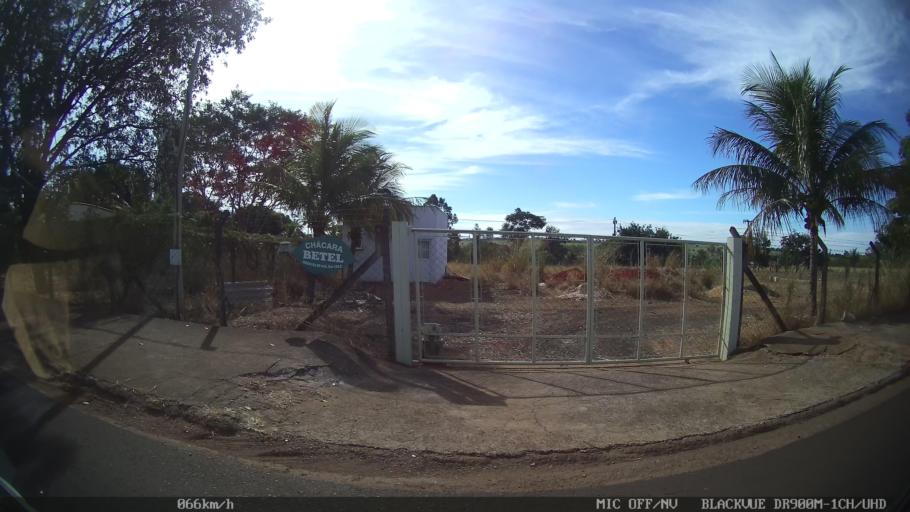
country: BR
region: Sao Paulo
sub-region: Guapiacu
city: Guapiacu
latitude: -20.7917
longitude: -49.3021
